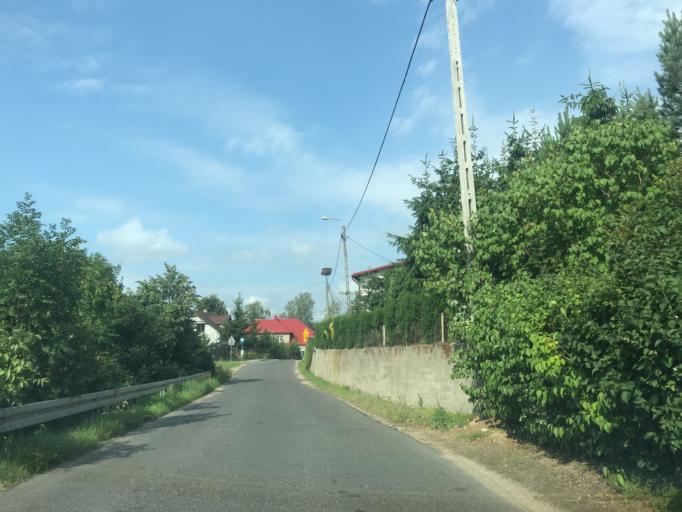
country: PL
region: Warmian-Masurian Voivodeship
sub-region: Powiat nowomiejski
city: Kurzetnik
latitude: 53.3718
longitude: 19.5598
